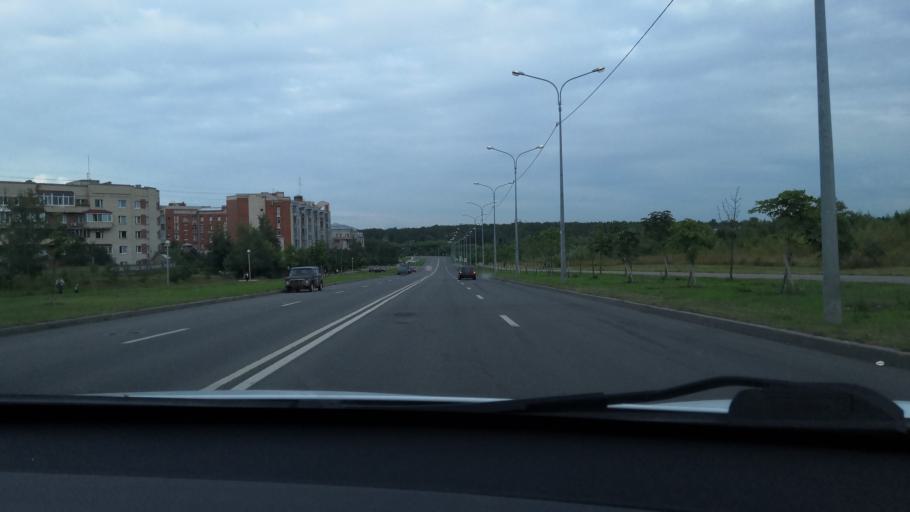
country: RU
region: St.-Petersburg
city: Pavlovsk
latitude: 59.6944
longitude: 30.4199
